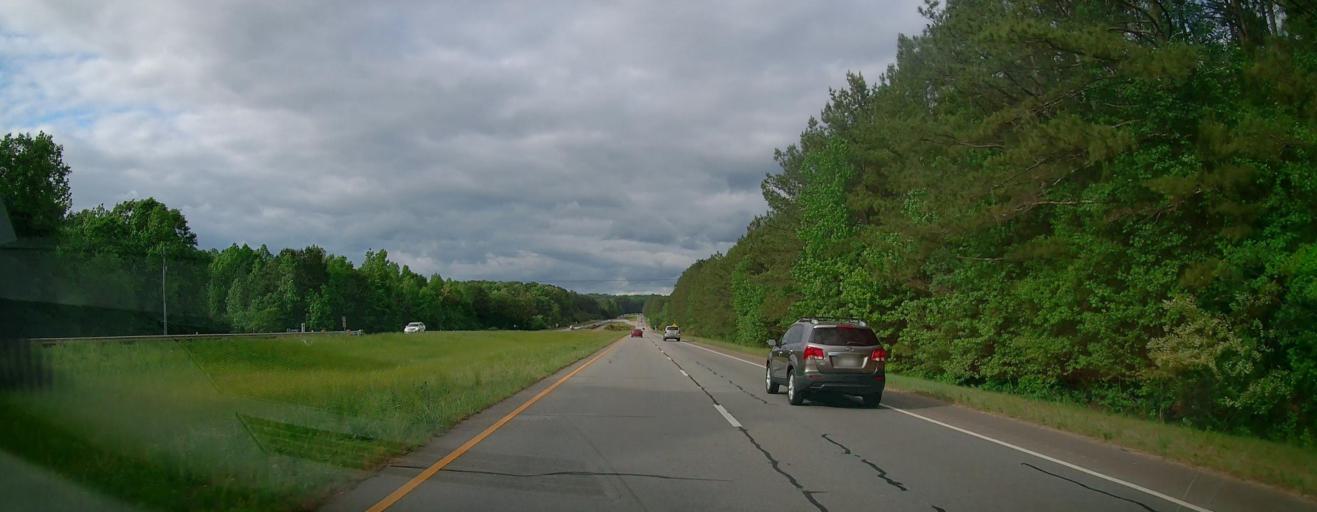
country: US
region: Georgia
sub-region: Barrow County
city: Statham
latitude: 33.8770
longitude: -83.5951
